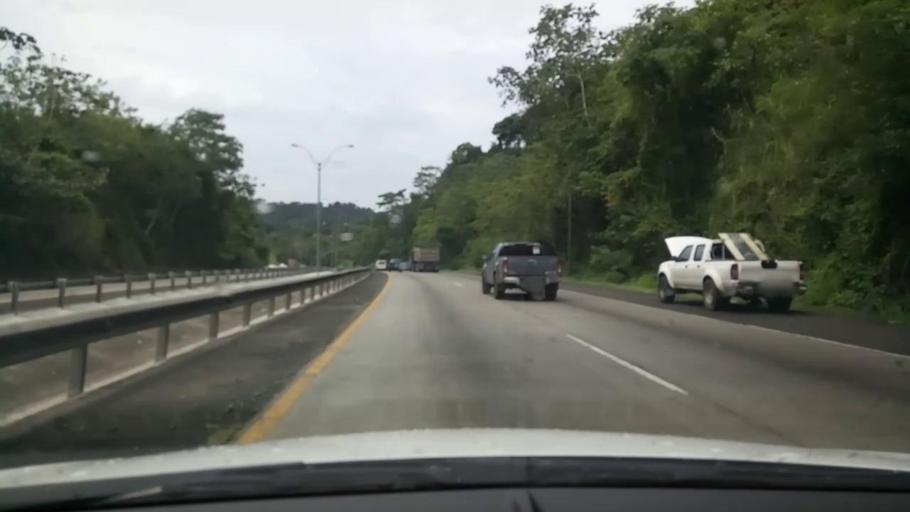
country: PA
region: Panama
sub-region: Distrito de Panama
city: Paraiso
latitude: 9.0351
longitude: -79.6175
